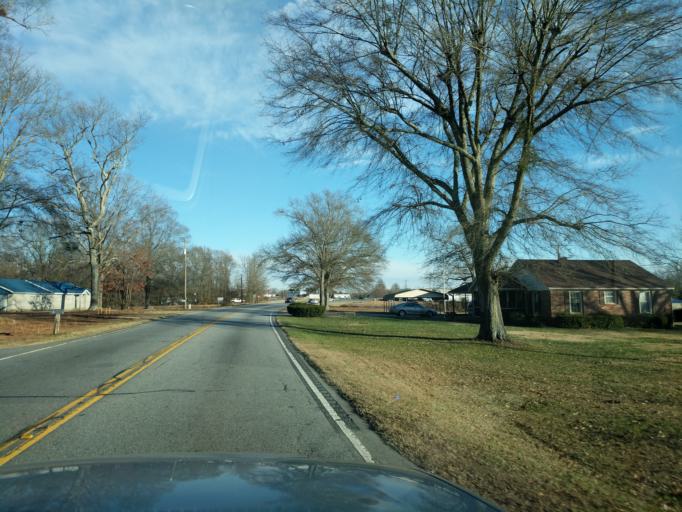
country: US
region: South Carolina
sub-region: Anderson County
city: Williamston
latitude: 34.6679
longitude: -82.5222
